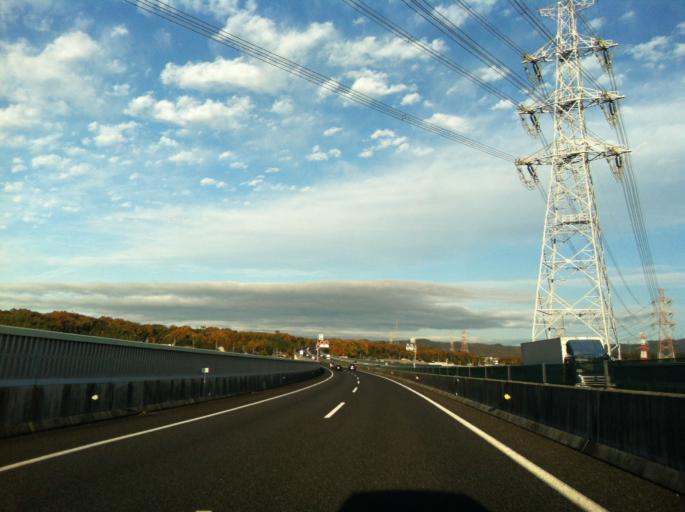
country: JP
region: Aichi
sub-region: Toyota-shi
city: Toyota
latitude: 35.1333
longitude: 137.1970
